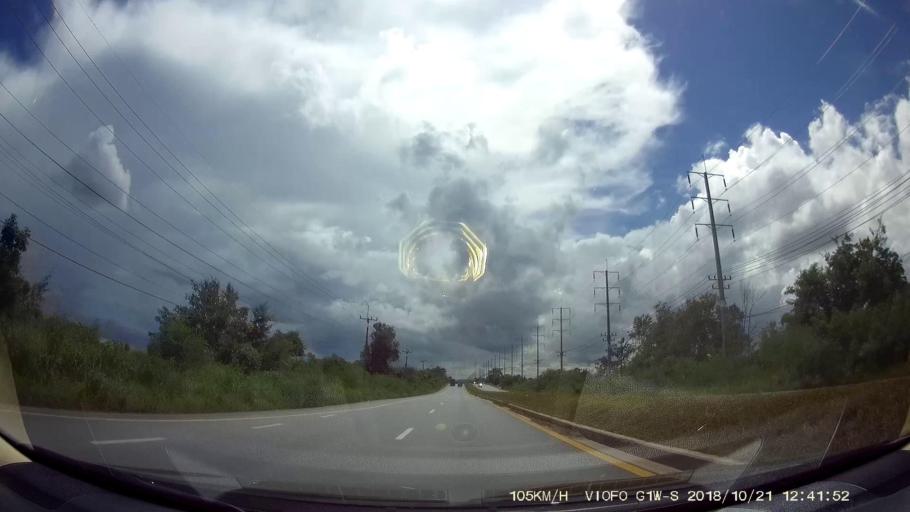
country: TH
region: Nakhon Ratchasima
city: Amphoe Sikhiu
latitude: 15.0063
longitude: 101.6860
